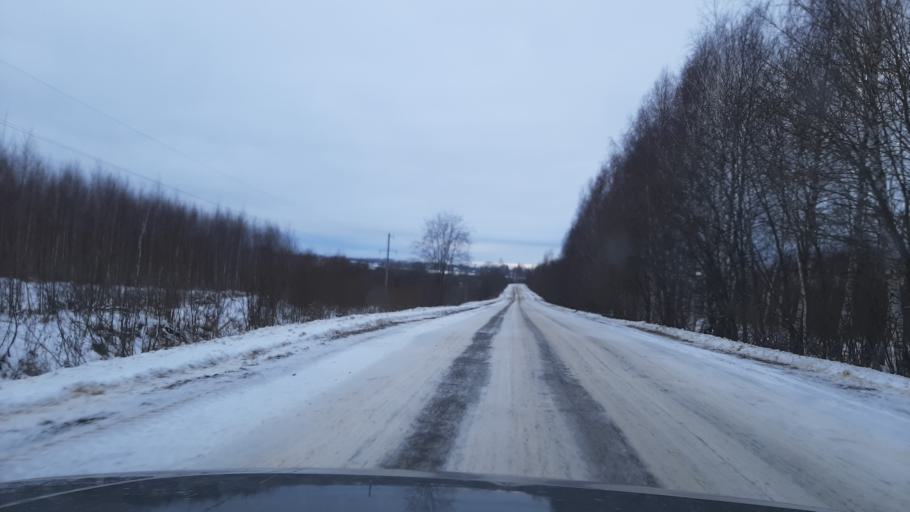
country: RU
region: Kostroma
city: Volgorechensk
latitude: 57.4408
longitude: 41.1169
